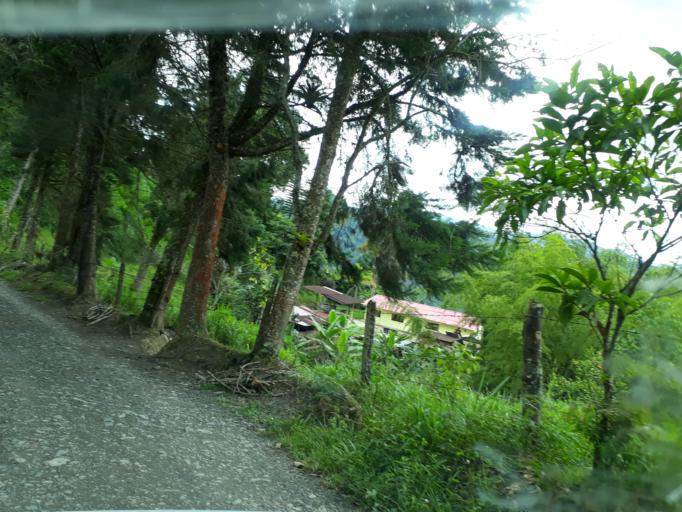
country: CO
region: Cundinamarca
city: Pacho
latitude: 5.1632
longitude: -74.2367
